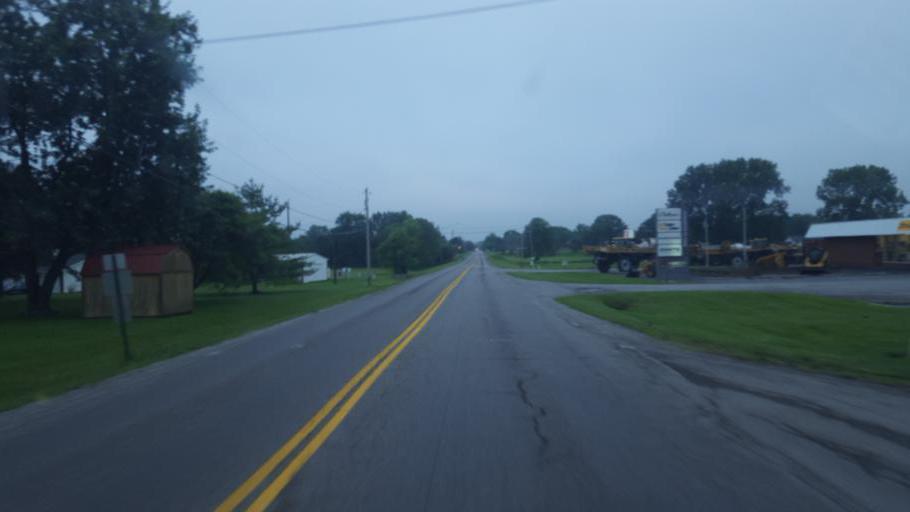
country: US
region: Ohio
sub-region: Fayette County
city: Washington Court House
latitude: 39.5408
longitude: -83.4112
